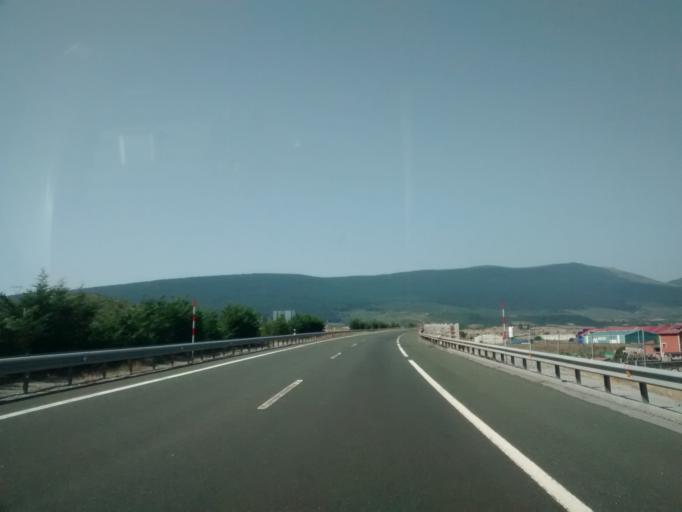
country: ES
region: Cantabria
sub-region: Provincia de Cantabria
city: Reinosa
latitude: 42.9788
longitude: -4.1468
